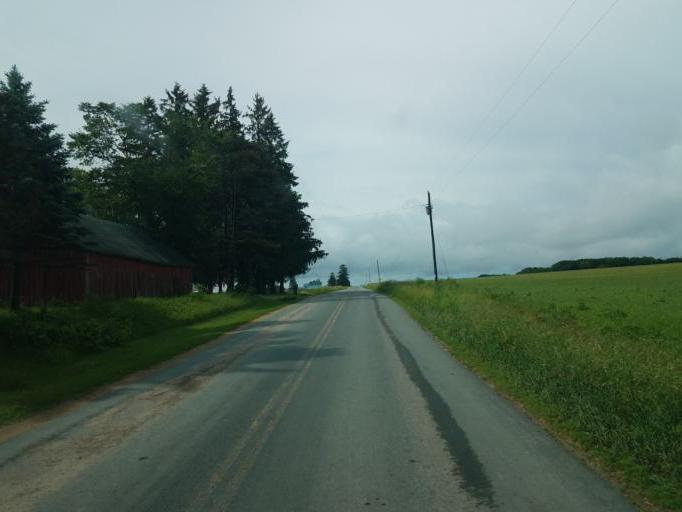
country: US
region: Wisconsin
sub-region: Vernon County
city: Hillsboro
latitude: 43.8001
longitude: -90.4433
